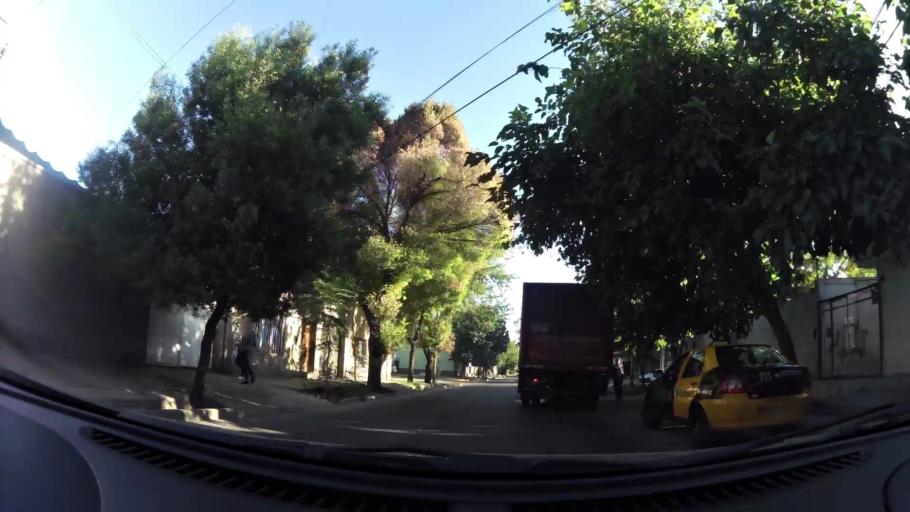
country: AR
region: Mendoza
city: Las Heras
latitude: -32.8704
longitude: -68.8275
